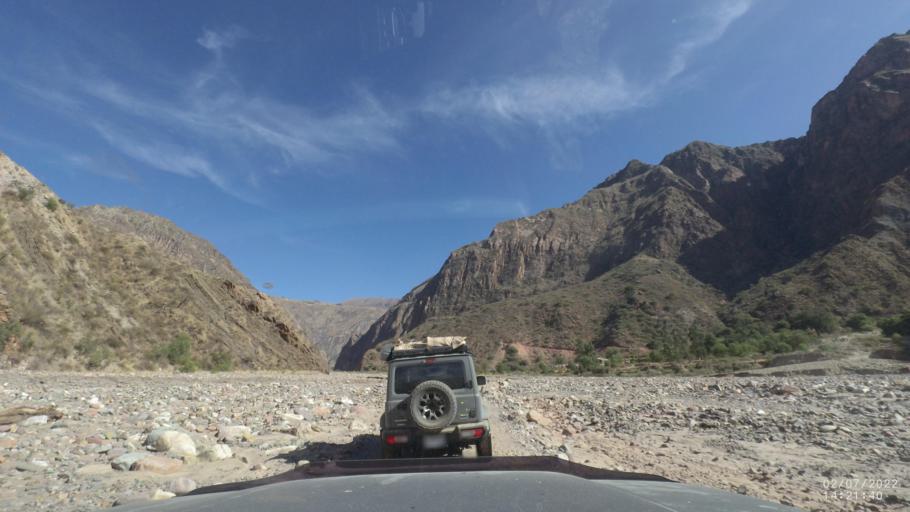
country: BO
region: Cochabamba
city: Irpa Irpa
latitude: -17.8292
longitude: -66.4126
